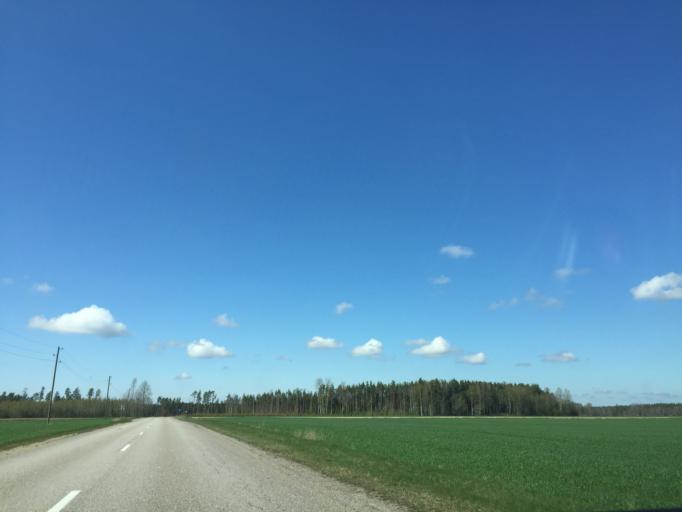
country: LV
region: Strenci
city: Seda
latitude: 57.5803
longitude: 25.7583
